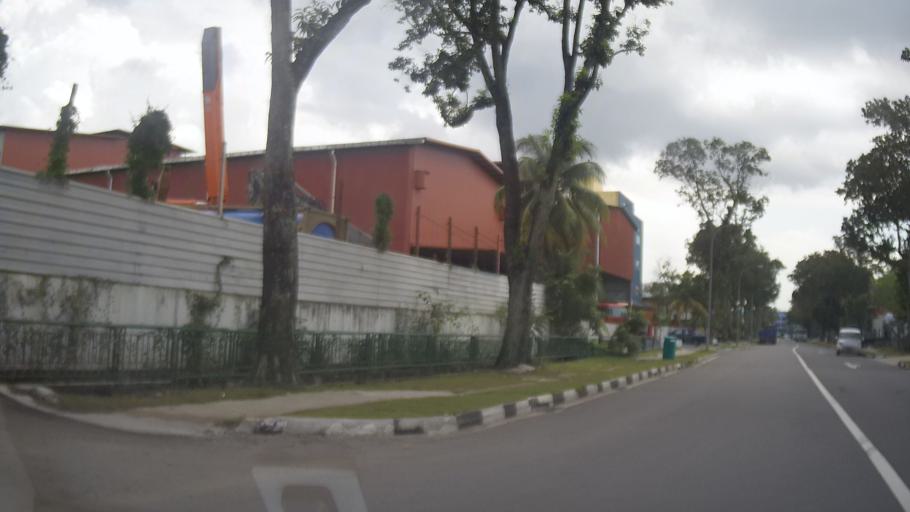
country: MY
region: Johor
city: Johor Bahru
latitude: 1.4156
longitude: 103.7430
